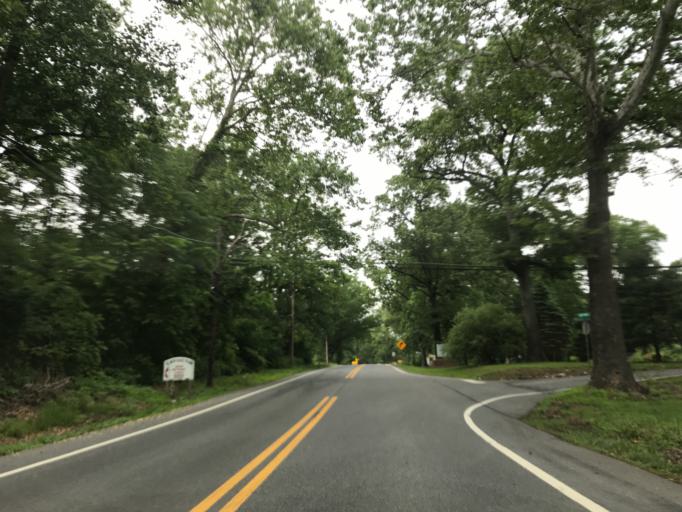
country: US
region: Maryland
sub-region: Frederick County
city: Thurmont
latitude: 39.5841
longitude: -77.4340
